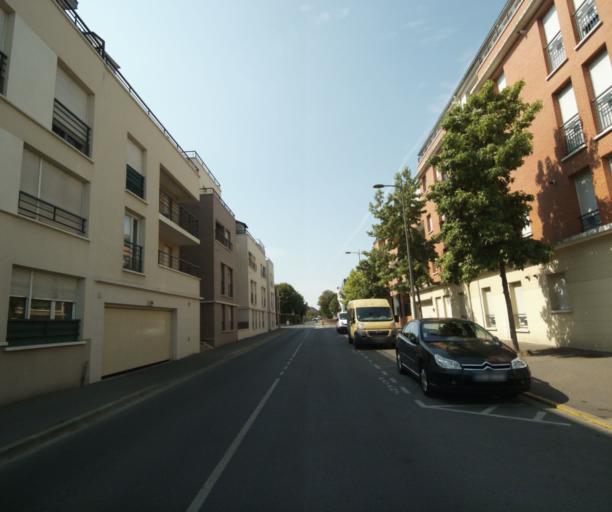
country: FR
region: Ile-de-France
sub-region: Departement des Yvelines
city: Conflans-Sainte-Honorine
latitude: 48.9986
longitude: 2.1020
